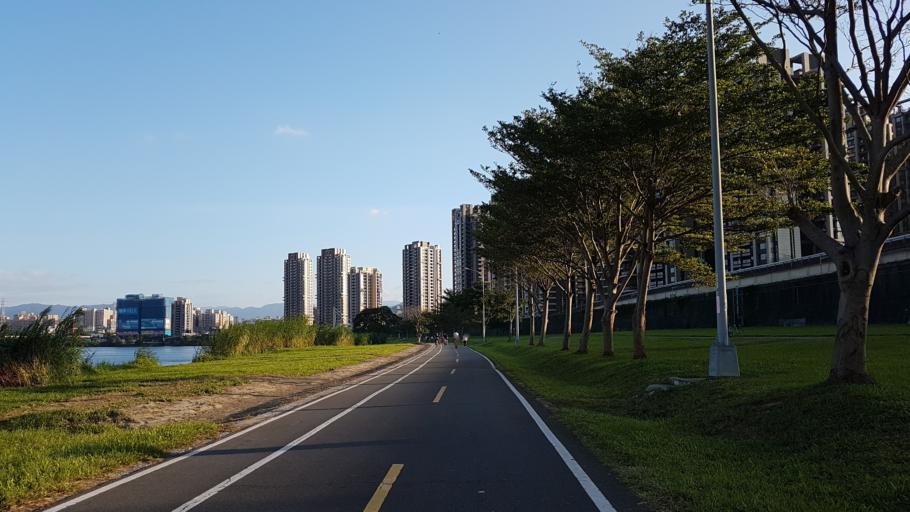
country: TW
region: Taipei
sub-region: Taipei
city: Banqiao
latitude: 25.0156
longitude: 121.4876
